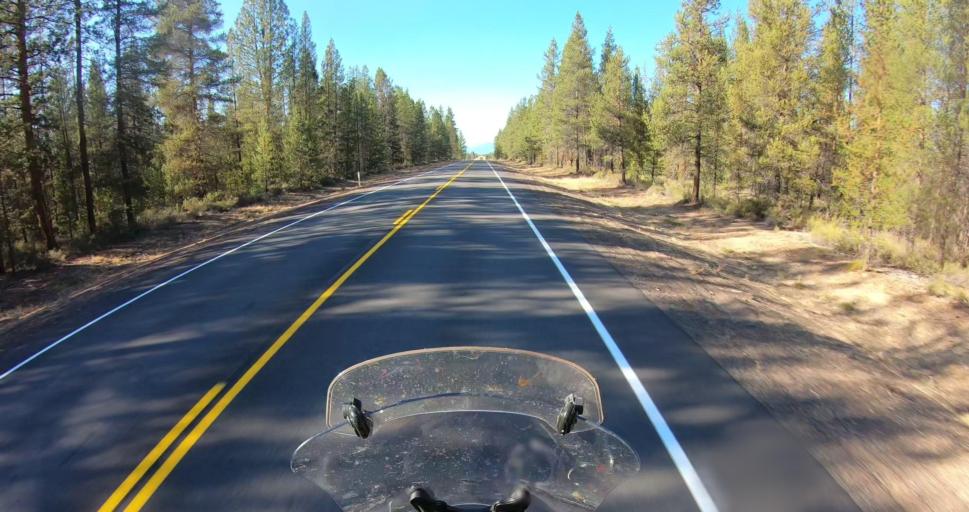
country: US
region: Oregon
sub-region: Deschutes County
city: La Pine
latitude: 43.5573
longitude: -121.4751
